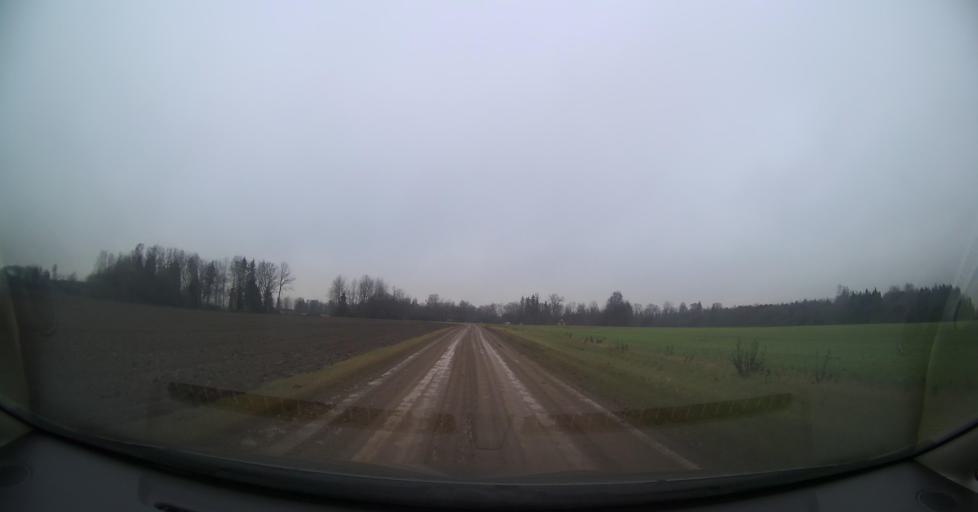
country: EE
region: Tartu
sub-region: Tartu linn
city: Tartu
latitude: 58.3908
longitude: 26.9282
